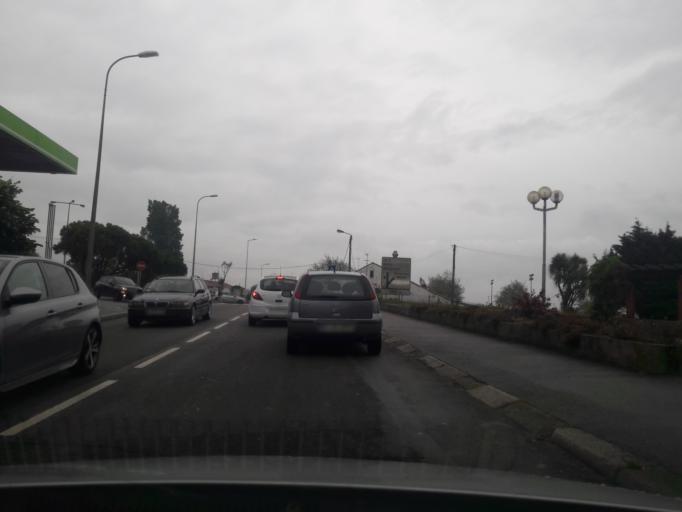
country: PT
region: Porto
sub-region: Vila do Conde
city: Vila do Conde
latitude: 41.3457
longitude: -8.7375
